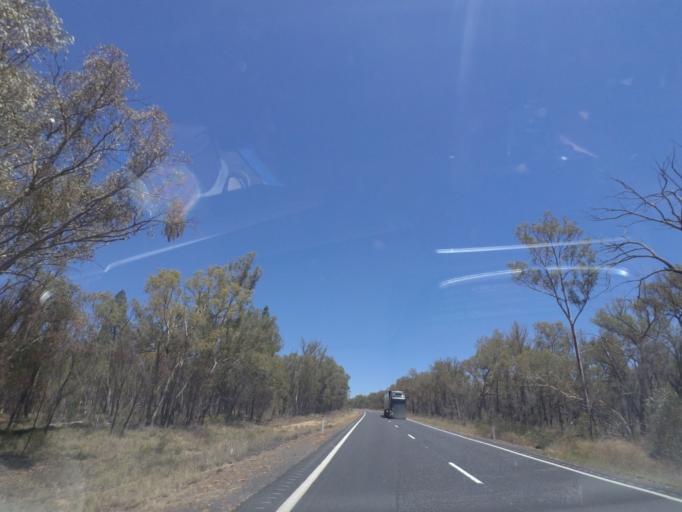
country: AU
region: New South Wales
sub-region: Warrumbungle Shire
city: Coonabarabran
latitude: -31.1761
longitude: 149.3578
